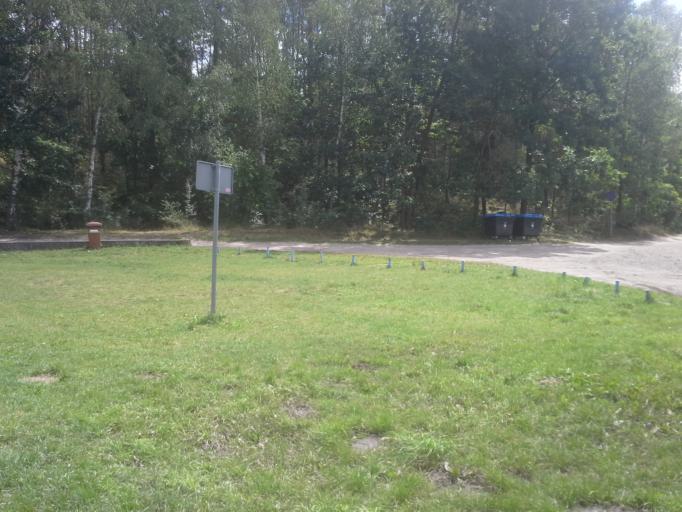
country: PL
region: Lubusz
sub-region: Powiat swiebodzinski
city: Miedzylesie
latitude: 52.2158
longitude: 15.3858
